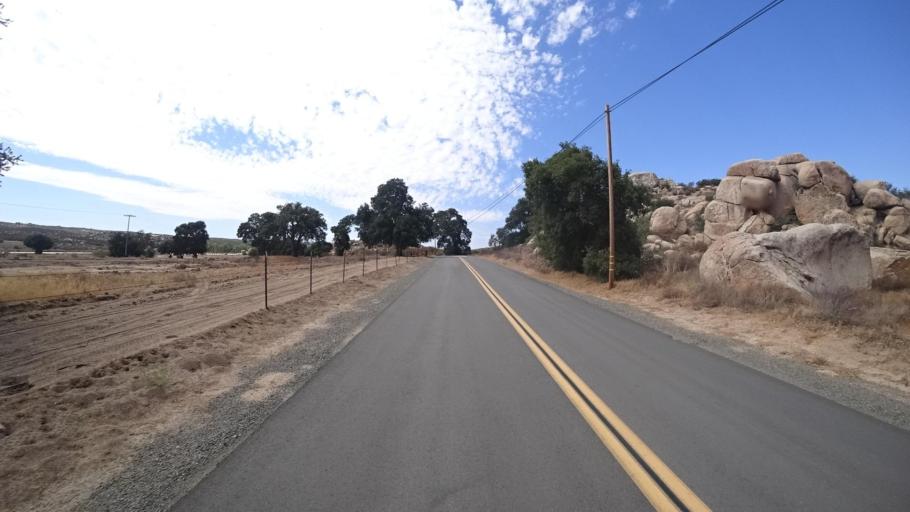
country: MX
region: Baja California
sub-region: Tecate
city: Cereso del Hongo
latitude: 32.6442
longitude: -116.2799
